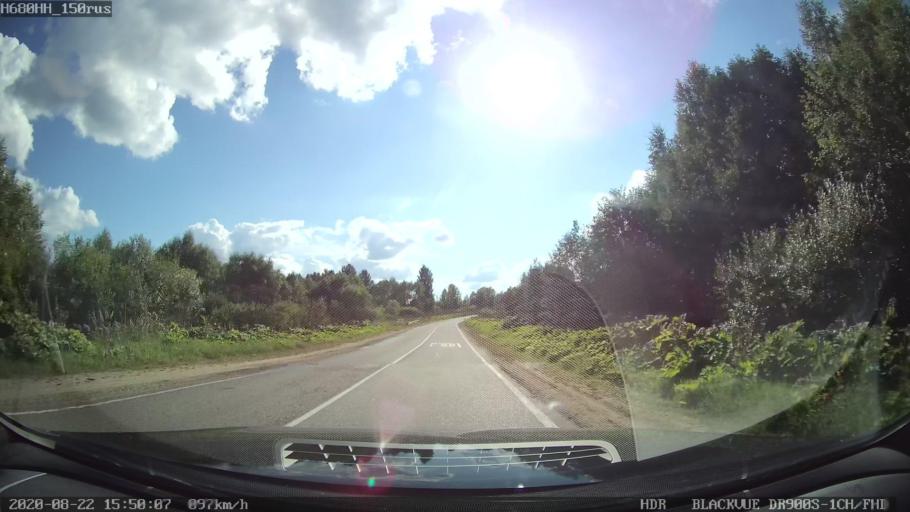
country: RU
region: Tverskaya
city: Bezhetsk
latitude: 57.6722
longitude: 36.4467
